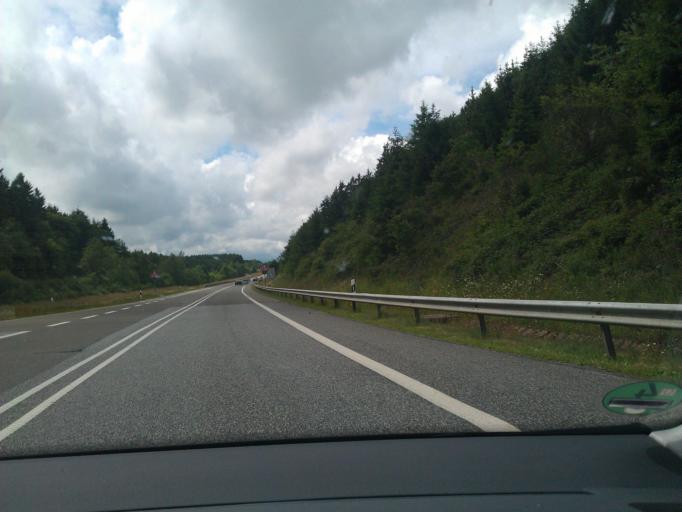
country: DE
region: Rheinland-Pfalz
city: Brandscheid
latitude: 50.2042
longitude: 6.3351
